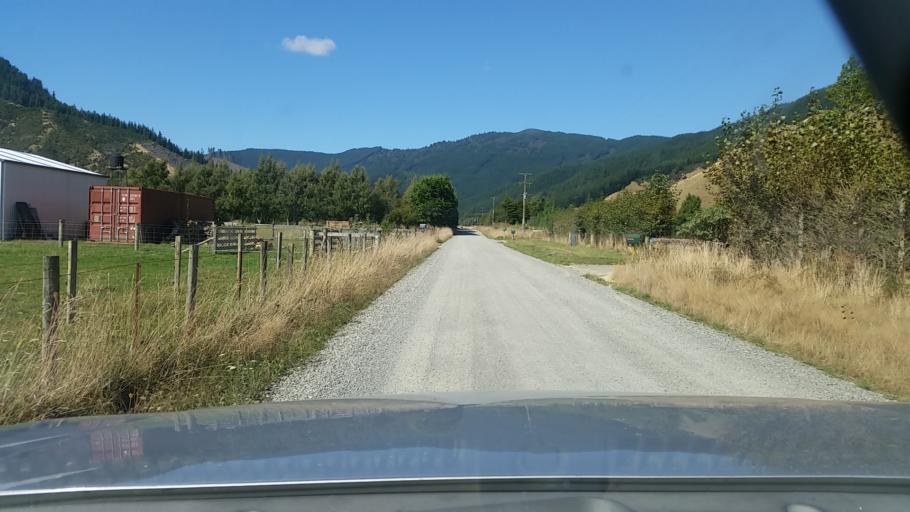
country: NZ
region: Marlborough
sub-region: Marlborough District
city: Blenheim
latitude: -41.4045
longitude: 173.7750
